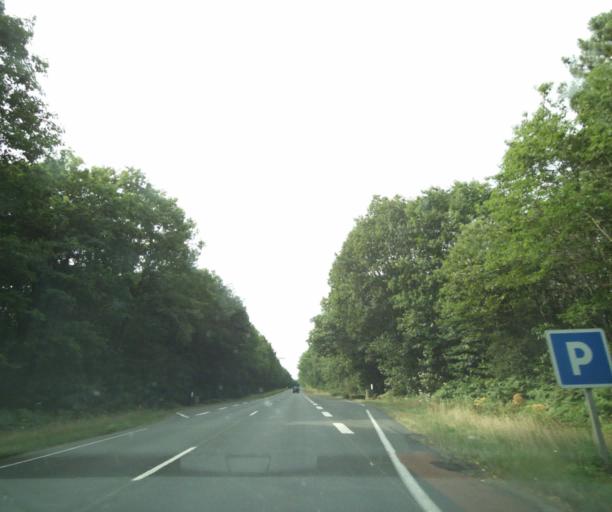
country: FR
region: Pays de la Loire
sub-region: Departement de la Sarthe
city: Marigne-Laille
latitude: 47.7663
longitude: 0.3521
